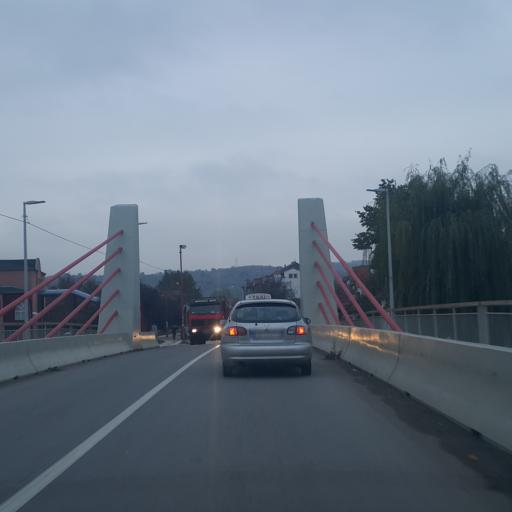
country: RS
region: Central Serbia
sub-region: Zajecarski Okrug
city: Zajecar
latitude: 43.9052
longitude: 22.2642
